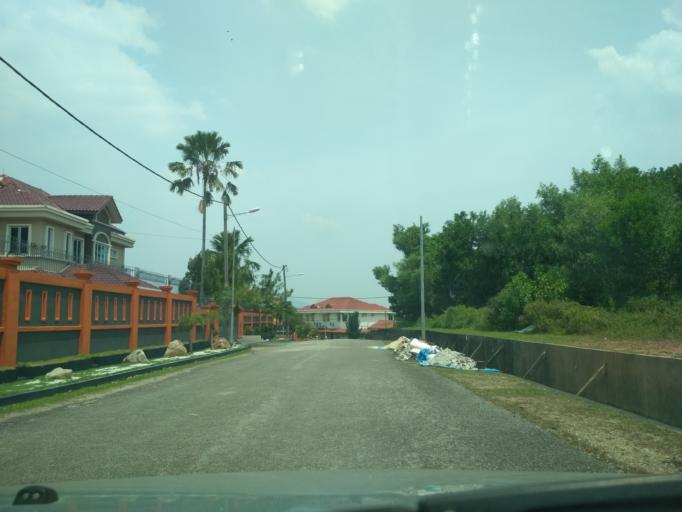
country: MY
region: Kedah
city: Kulim
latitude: 5.3629
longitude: 100.5335
